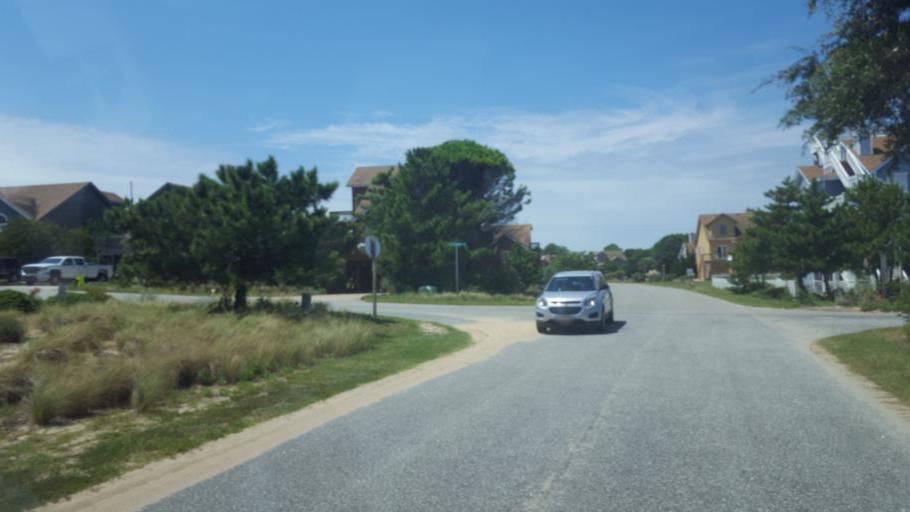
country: US
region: North Carolina
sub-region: Dare County
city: Nags Head
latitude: 35.9506
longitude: -75.6254
